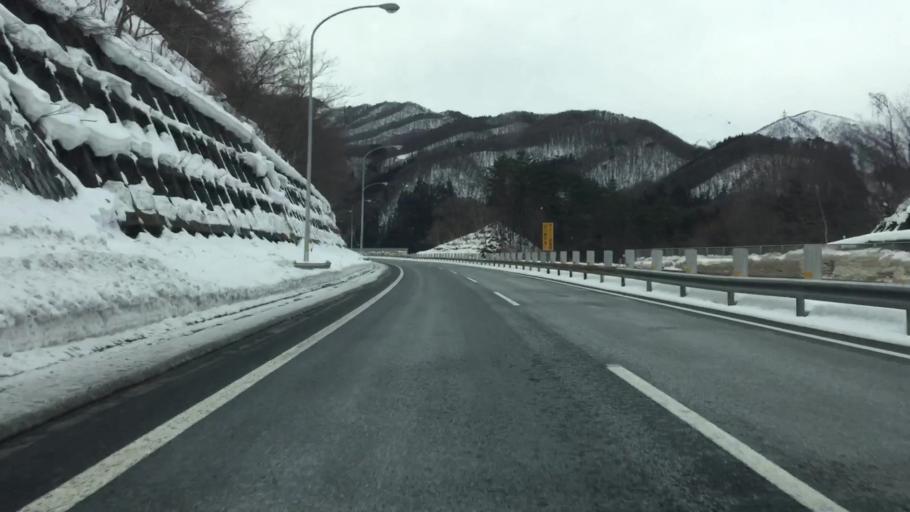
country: JP
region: Gunma
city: Numata
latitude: 36.7689
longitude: 138.9618
